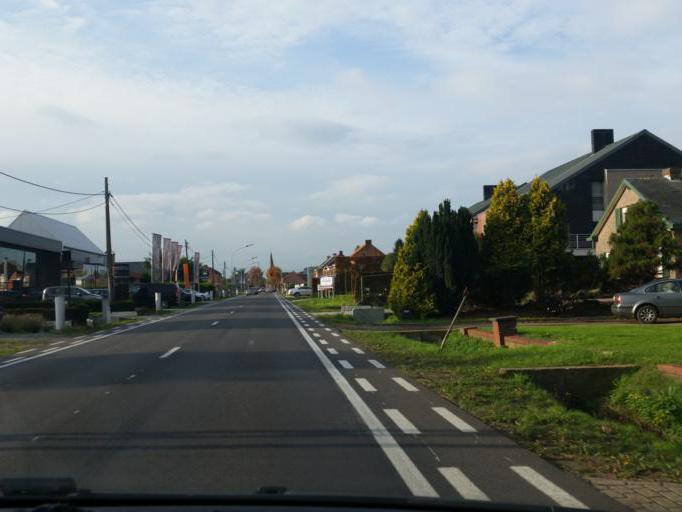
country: BE
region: Flanders
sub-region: Provincie Antwerpen
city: Berlaar
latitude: 51.0791
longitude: 4.6762
